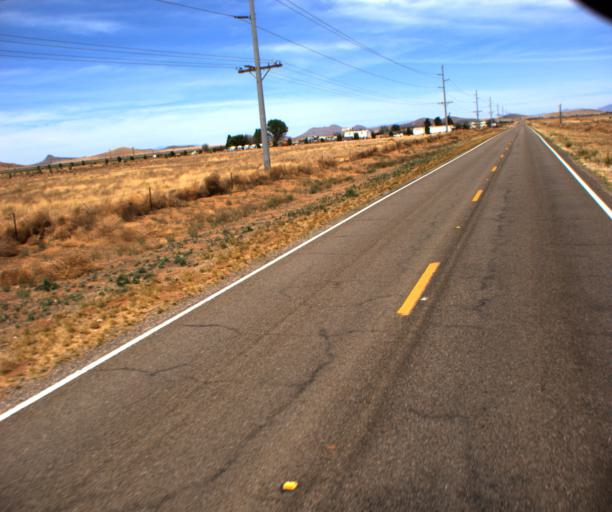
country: US
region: Arizona
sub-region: Cochise County
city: Tombstone
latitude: 31.8368
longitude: -109.6952
